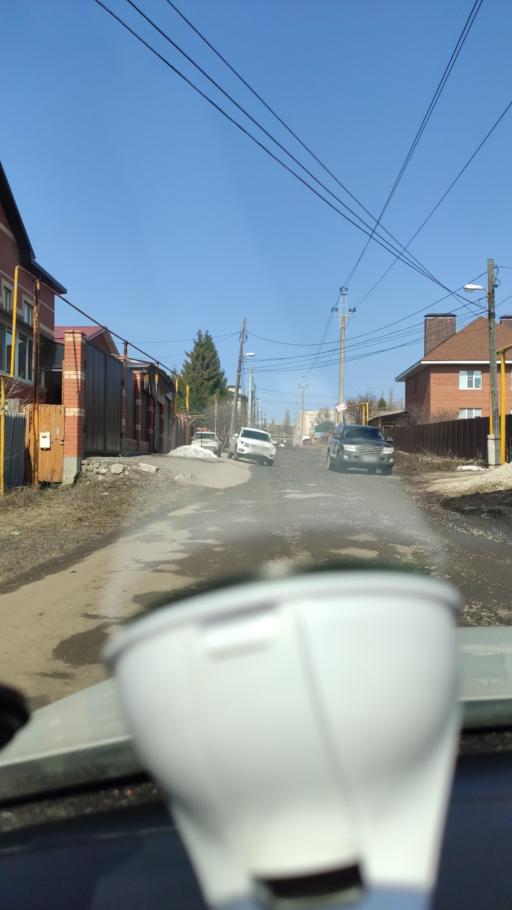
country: RU
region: Samara
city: Petra-Dubrava
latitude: 53.2939
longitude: 50.2811
